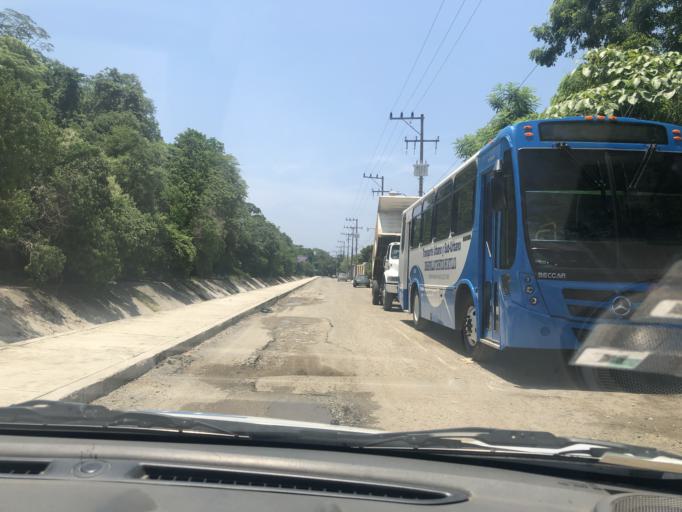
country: MX
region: Oaxaca
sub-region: Santa Maria Huatulco
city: Sector H Tres
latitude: 15.7790
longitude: -96.1515
